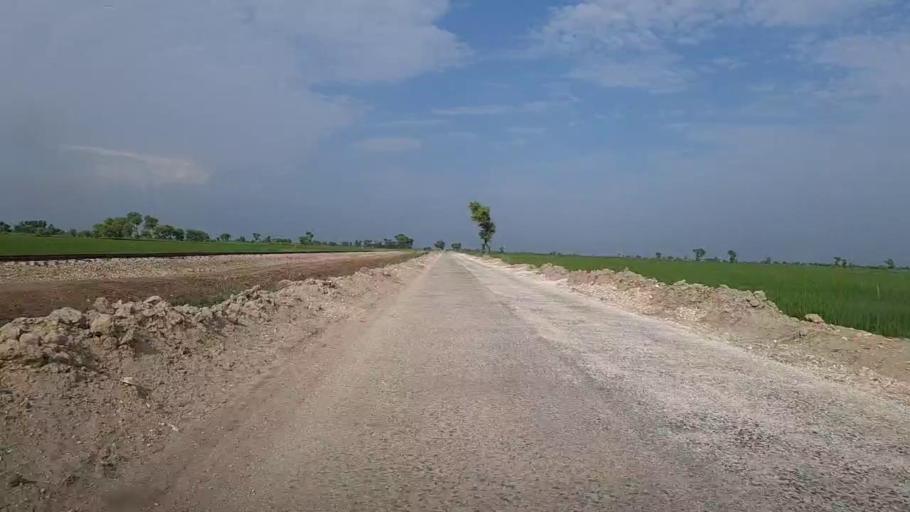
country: PK
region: Sindh
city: Thul
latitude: 28.2662
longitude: 68.8263
